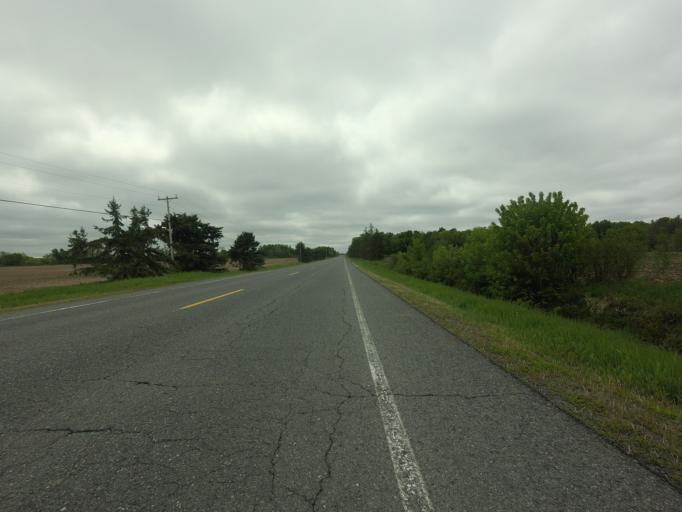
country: CA
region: Ontario
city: Casselman
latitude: 45.0431
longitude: -75.1940
